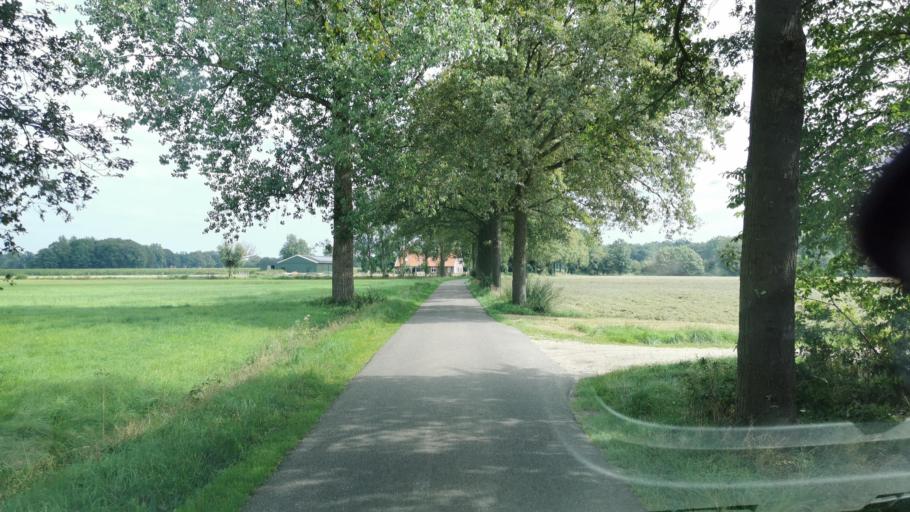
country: NL
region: Overijssel
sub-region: Gemeente Oldenzaal
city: Oldenzaal
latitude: 52.3470
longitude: 6.8771
